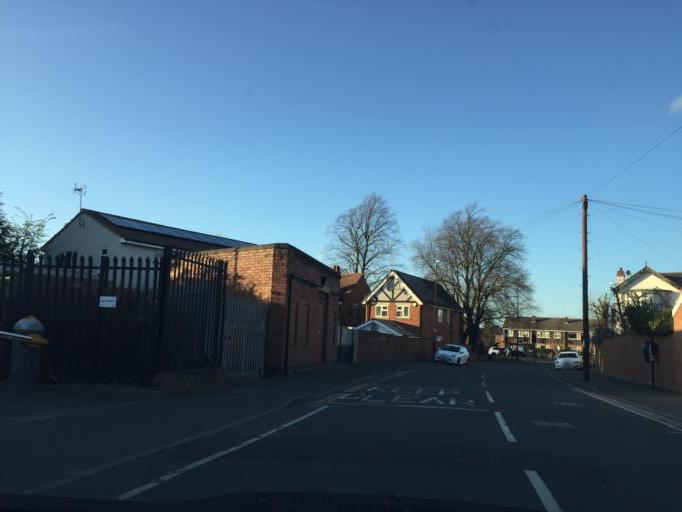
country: GB
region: England
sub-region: Coventry
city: Coventry
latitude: 52.4050
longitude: -1.4660
